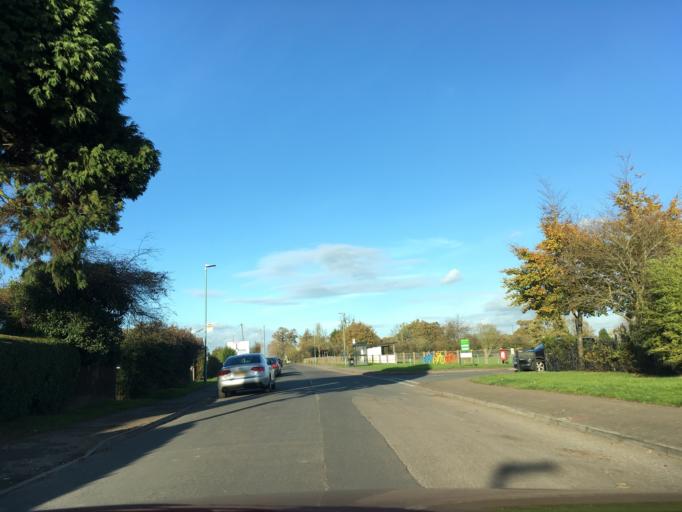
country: GB
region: England
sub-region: Gloucestershire
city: Berkeley
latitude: 51.6953
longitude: -2.4587
